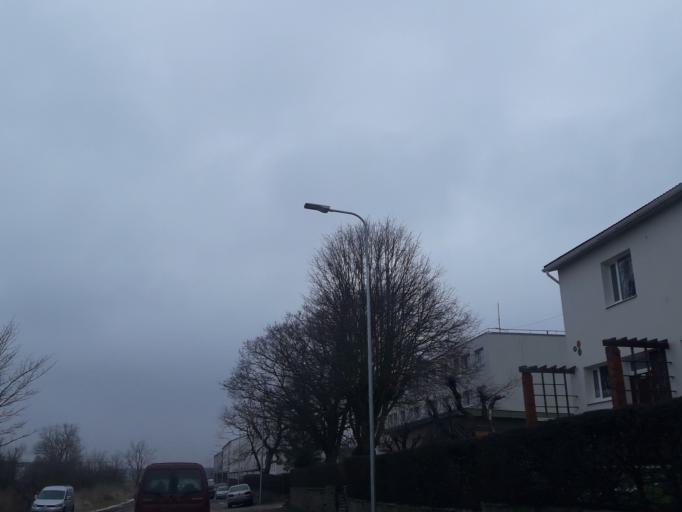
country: EE
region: Saare
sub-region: Kuressaare linn
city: Kuressaare
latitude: 58.2596
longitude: 22.4799
